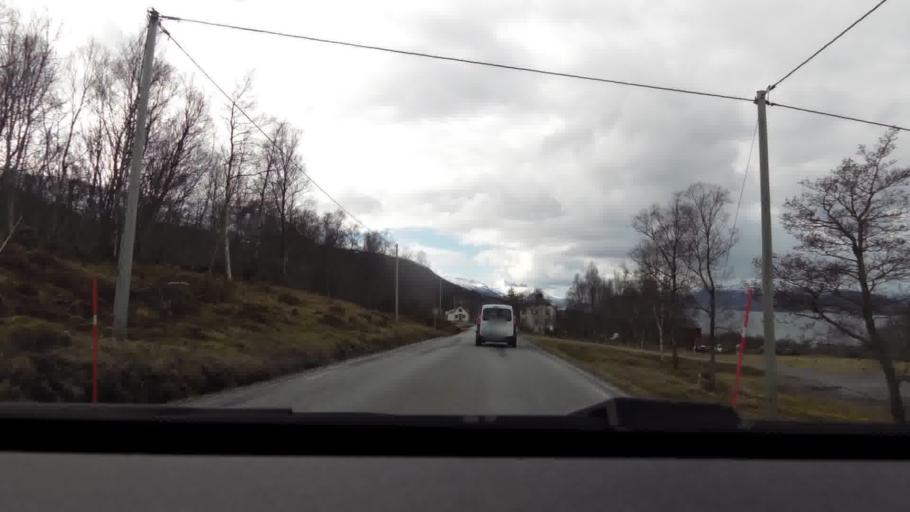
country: NO
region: More og Romsdal
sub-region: Gjemnes
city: Batnfjordsora
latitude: 62.9514
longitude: 7.6458
